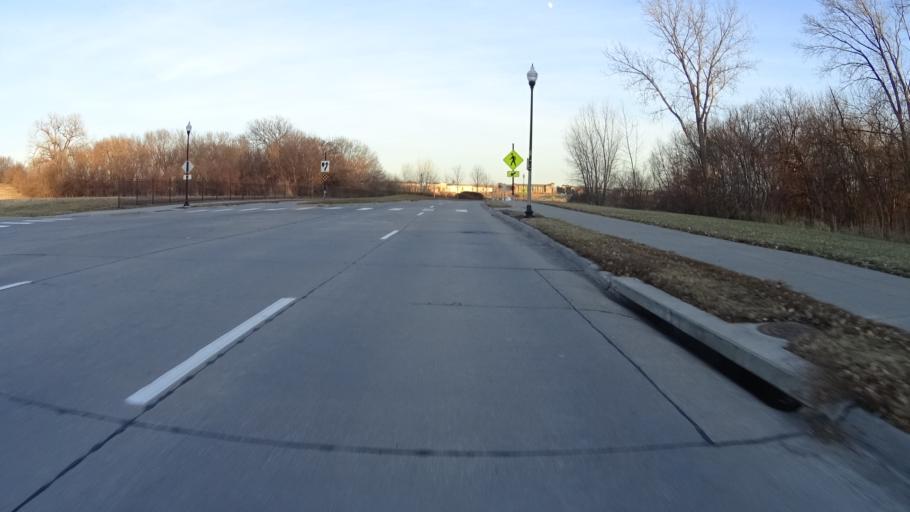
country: US
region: Nebraska
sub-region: Sarpy County
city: Papillion
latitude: 41.1330
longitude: -96.0363
